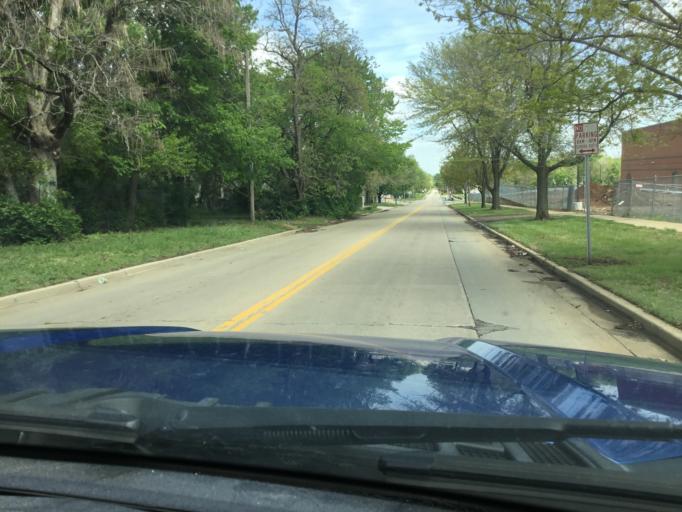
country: US
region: Kansas
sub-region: Shawnee County
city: Topeka
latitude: 39.0172
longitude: -95.6609
